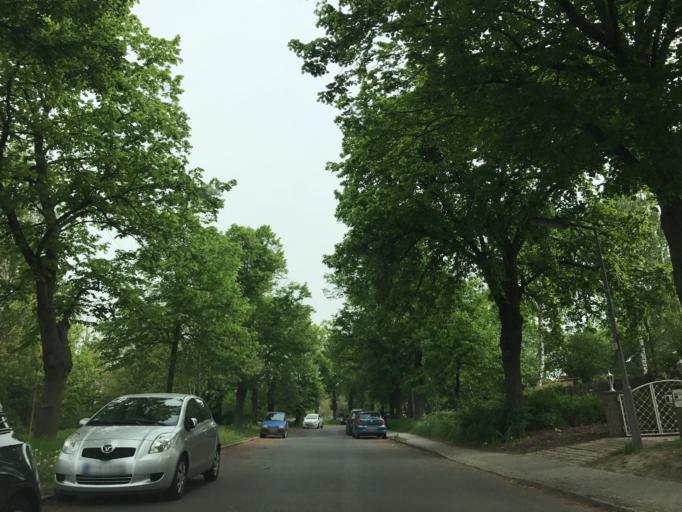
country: DE
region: Berlin
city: Staaken
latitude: 52.5270
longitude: 13.1439
